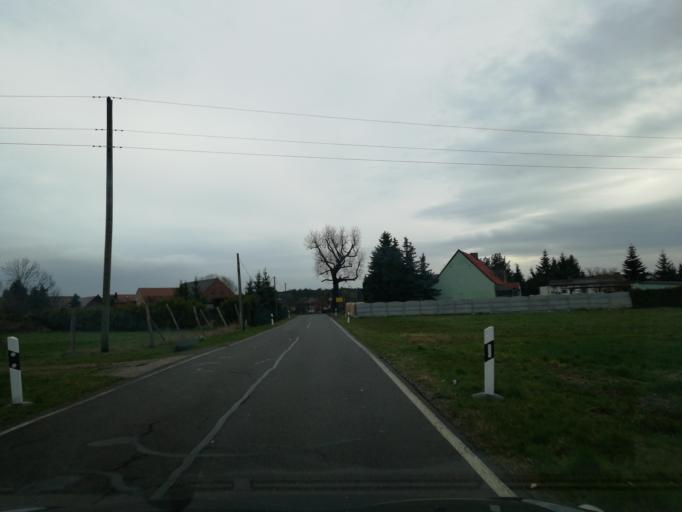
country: DE
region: Brandenburg
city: Calau
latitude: 51.7322
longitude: 14.0162
